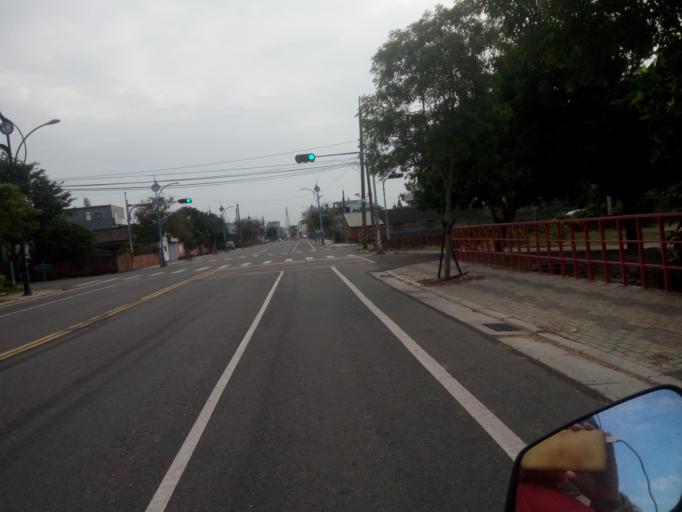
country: TW
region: Taiwan
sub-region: Chiayi
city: Taibao
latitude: 23.4870
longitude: 120.3357
